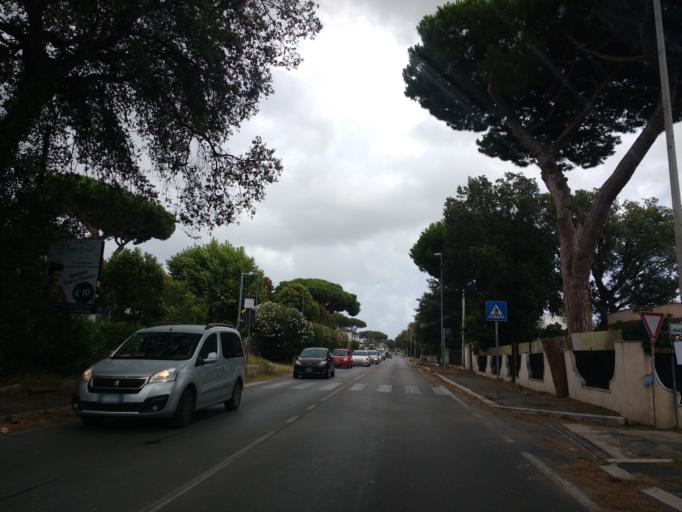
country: IT
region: Latium
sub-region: Citta metropolitana di Roma Capitale
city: Anzio
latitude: 41.4861
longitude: 12.6001
